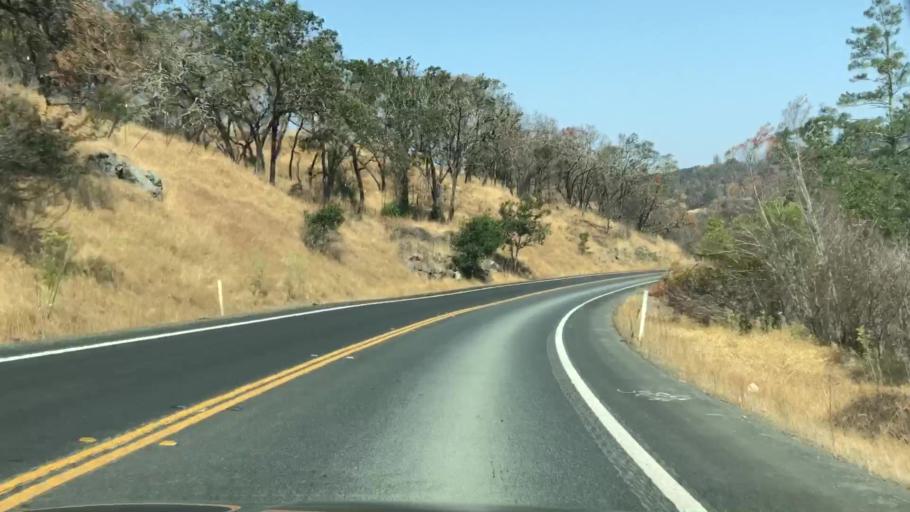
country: US
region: California
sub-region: Sonoma County
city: Larkfield-Wikiup
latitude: 38.5539
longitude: -122.6745
